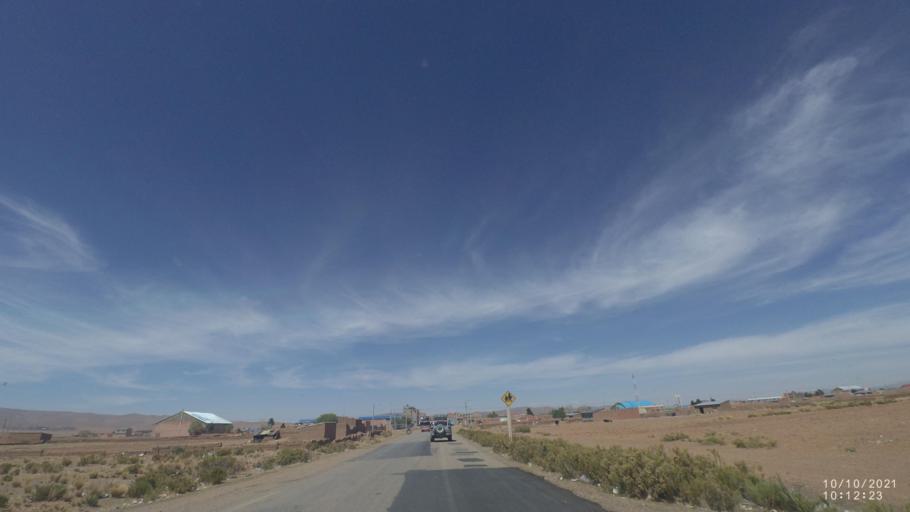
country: BO
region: La Paz
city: Eucaliptus
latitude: -17.4343
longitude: -67.5142
